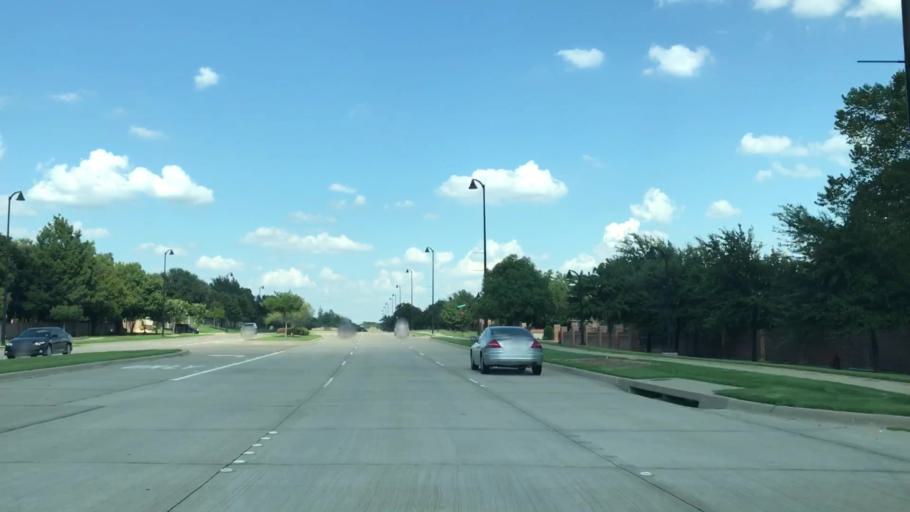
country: US
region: Texas
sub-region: Tarrant County
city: Keller
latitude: 32.9009
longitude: -97.2094
